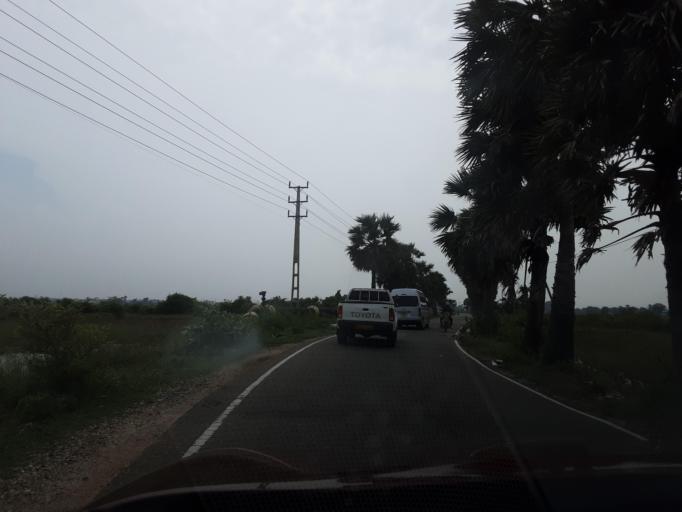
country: LK
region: Northern Province
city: Jaffna
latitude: 9.6660
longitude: 80.0580
